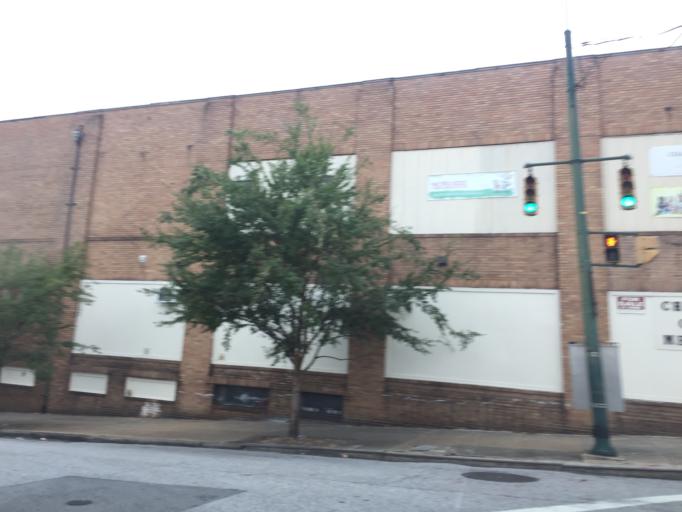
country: US
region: Maryland
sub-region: City of Baltimore
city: Baltimore
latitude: 39.2861
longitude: -76.6483
